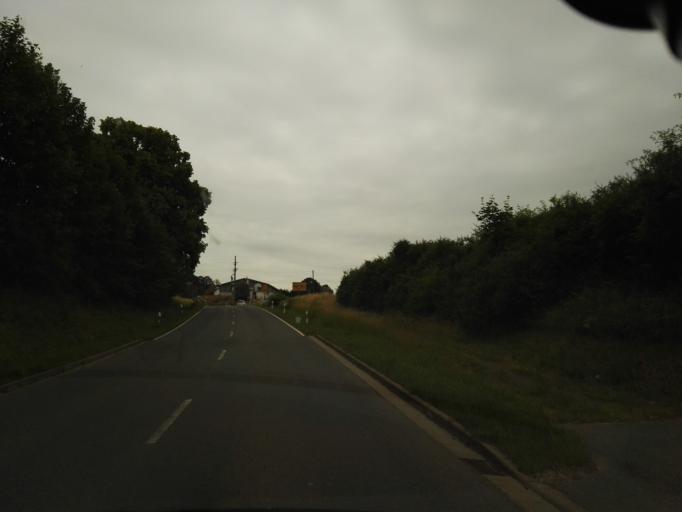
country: DE
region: Bavaria
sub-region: Upper Franconia
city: Redwitz an der Rodach
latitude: 50.1677
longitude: 11.2032
